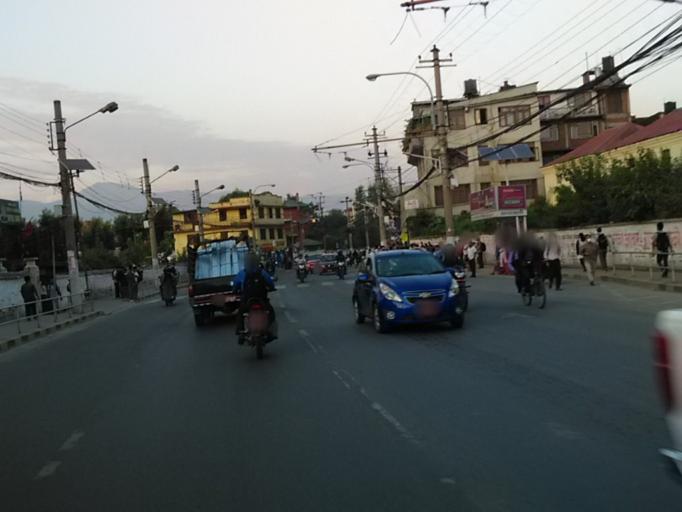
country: NP
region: Central Region
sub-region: Bagmati Zone
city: Kathmandu
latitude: 27.6938
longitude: 85.3191
